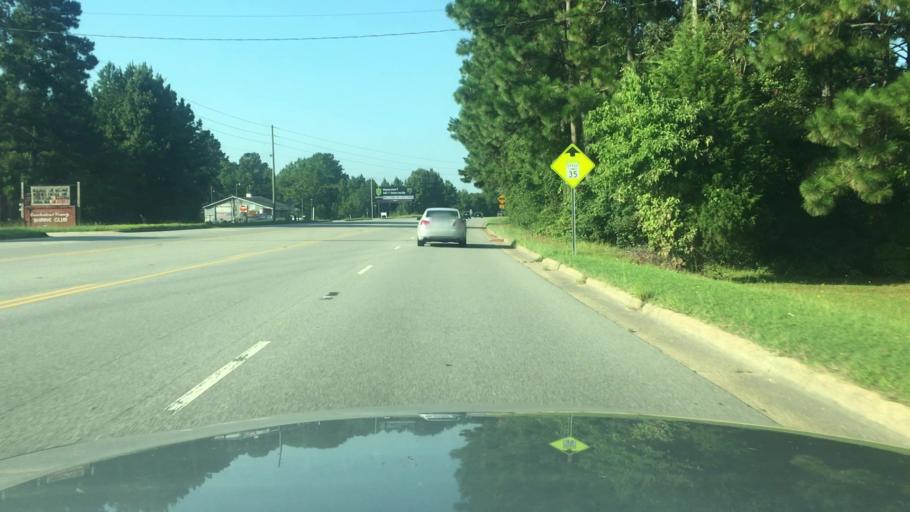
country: US
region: North Carolina
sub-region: Cumberland County
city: Eastover
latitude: 35.1841
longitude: -78.8534
